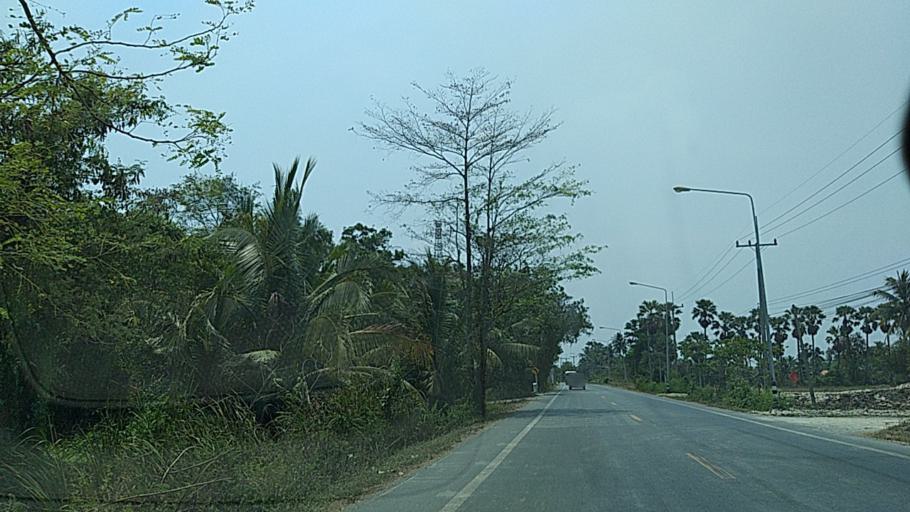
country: TH
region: Chachoengsao
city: Bang Nam Priao
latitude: 13.8813
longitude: 100.9685
